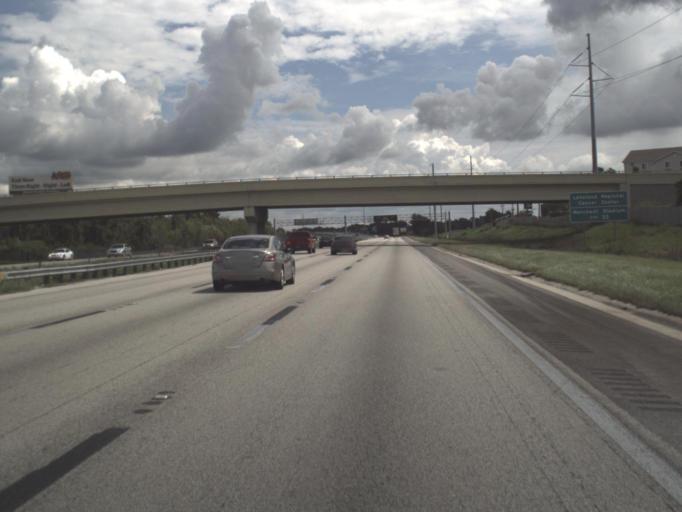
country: US
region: Florida
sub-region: Polk County
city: Gibsonia
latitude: 28.0927
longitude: -81.9594
